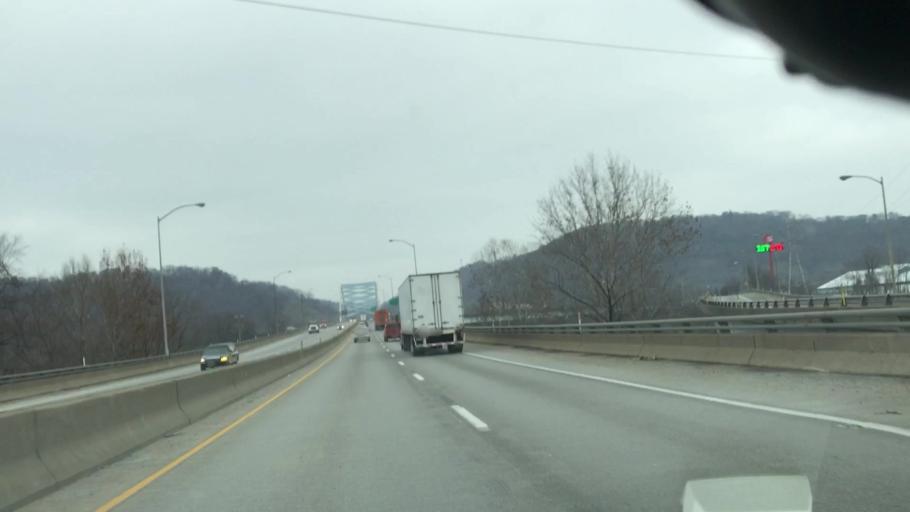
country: US
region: Pennsylvania
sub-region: Allegheny County
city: Coraopolis
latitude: 40.5084
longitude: -80.1378
